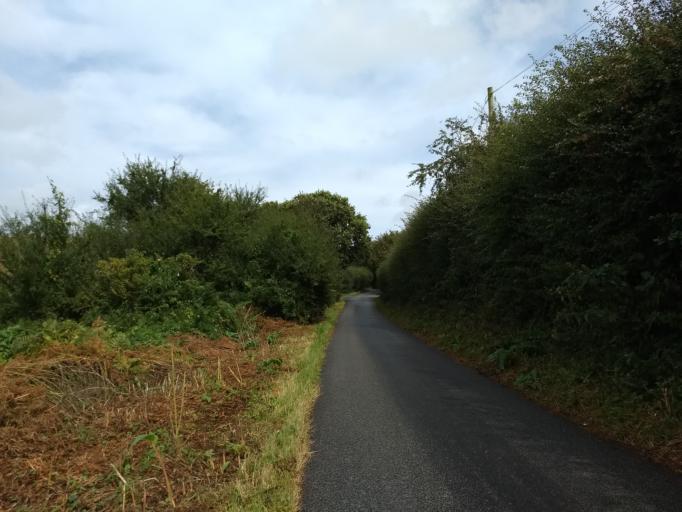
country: GB
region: England
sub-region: Isle of Wight
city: Newchurch
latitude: 50.6418
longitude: -1.2295
